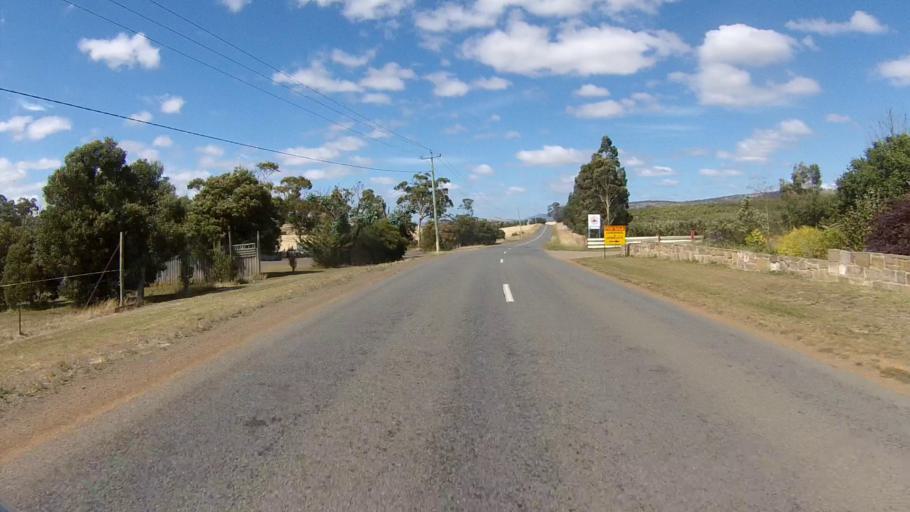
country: AU
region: Tasmania
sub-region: Sorell
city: Sorell
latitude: -42.6497
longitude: 147.4341
